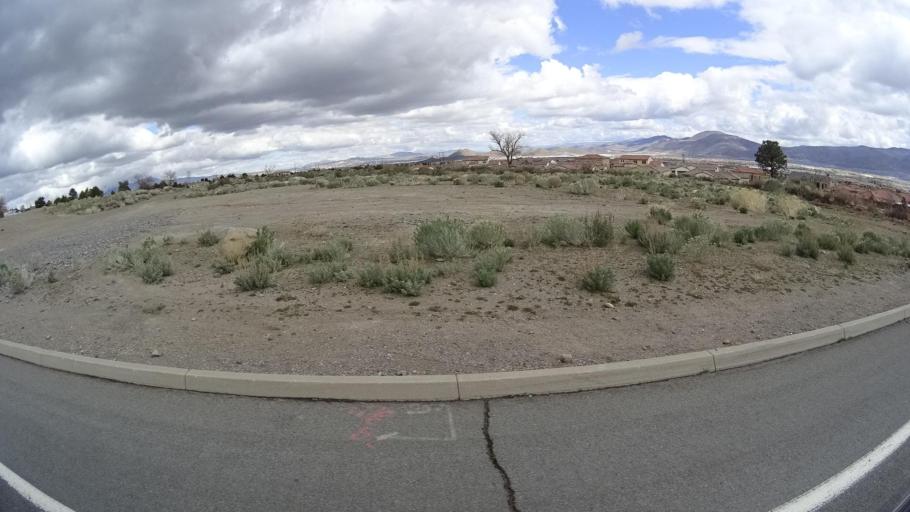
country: US
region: Nevada
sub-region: Washoe County
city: Sparks
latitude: 39.4040
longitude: -119.7714
